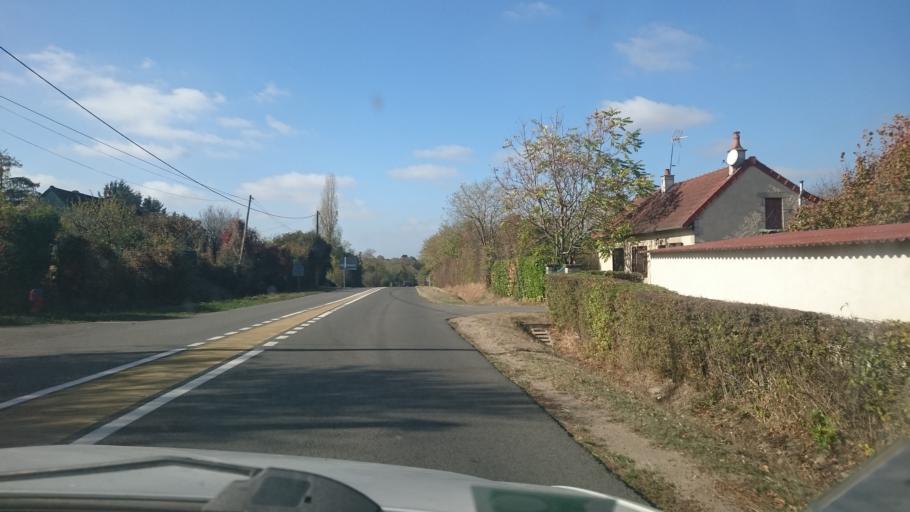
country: FR
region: Auvergne
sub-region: Departement de l'Allier
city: Neuvy
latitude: 46.5534
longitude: 3.2623
